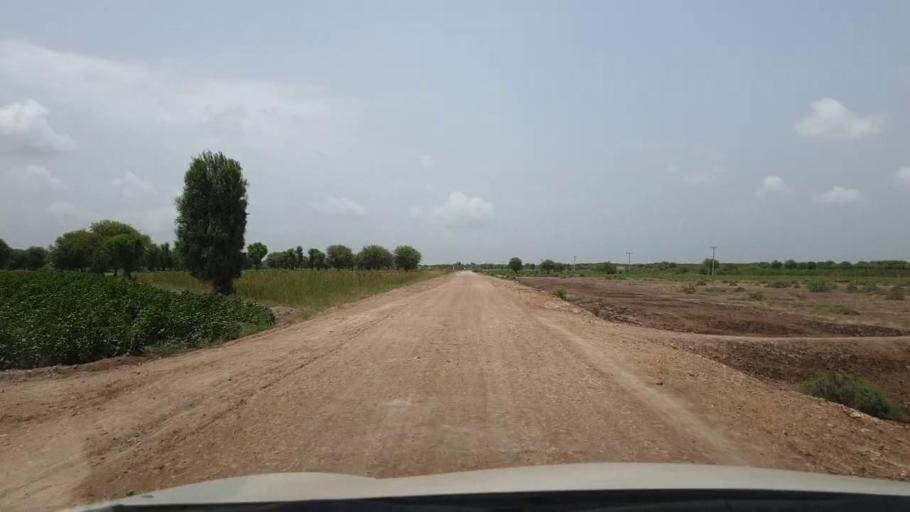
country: PK
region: Sindh
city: Chambar
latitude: 25.2029
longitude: 68.7626
